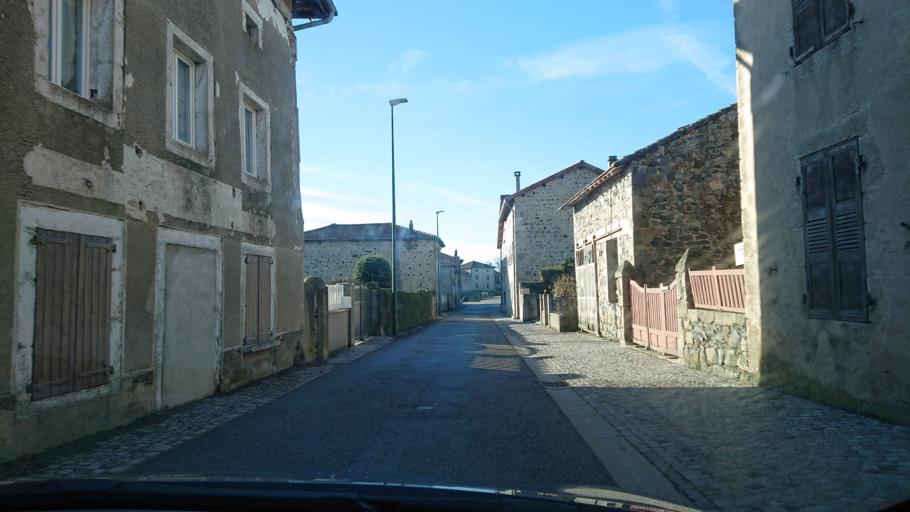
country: FR
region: Auvergne
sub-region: Departement de la Haute-Loire
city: Vorey
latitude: 45.2213
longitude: 3.9409
